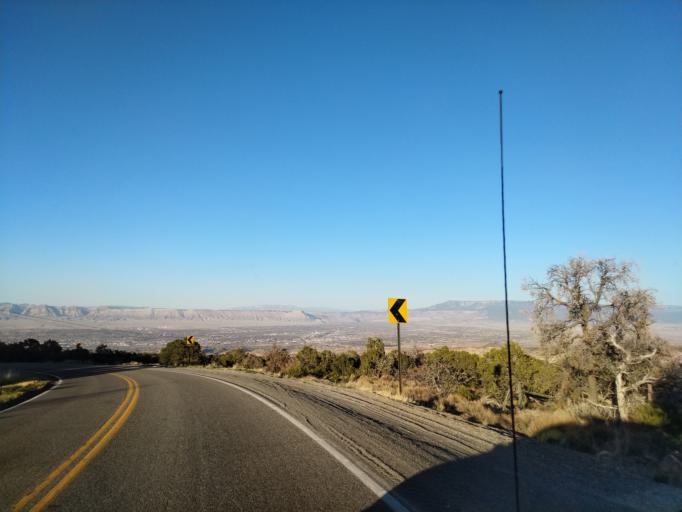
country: US
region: Colorado
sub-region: Mesa County
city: Redlands
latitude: 39.0183
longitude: -108.6605
